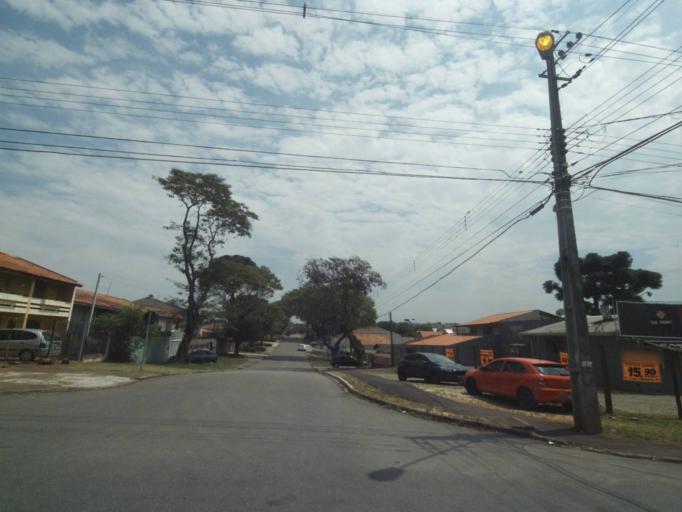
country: BR
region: Parana
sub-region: Pinhais
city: Pinhais
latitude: -25.4104
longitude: -49.2047
